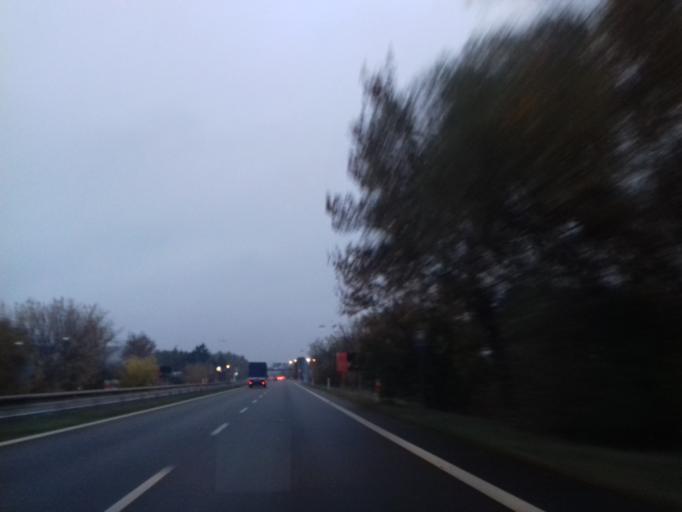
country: CZ
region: Olomoucky
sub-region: Okres Olomouc
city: Olomouc
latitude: 49.6017
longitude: 17.2254
